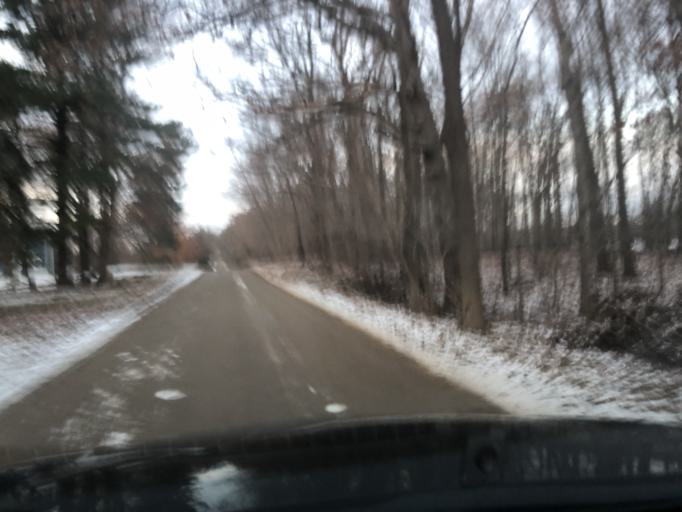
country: US
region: Michigan
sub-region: Oakland County
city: Milford
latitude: 42.5882
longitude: -83.6401
